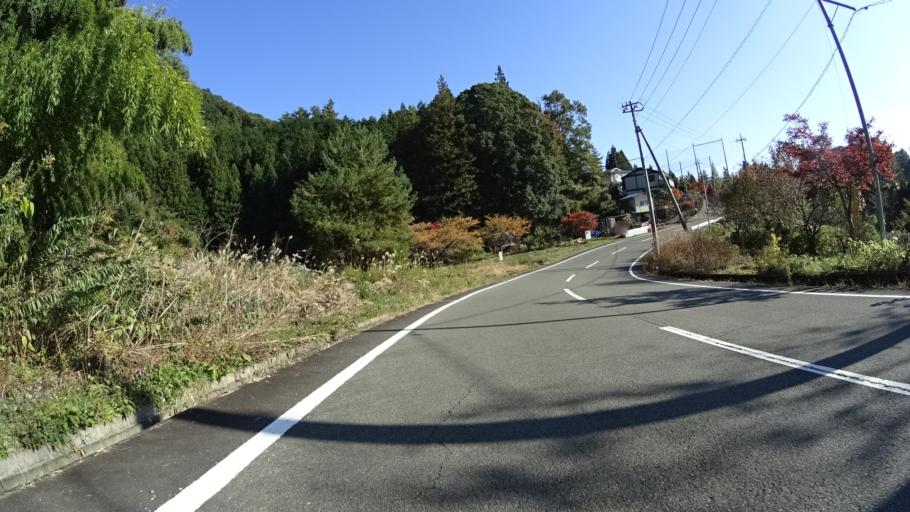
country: JP
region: Yamanashi
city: Uenohara
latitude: 35.6625
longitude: 139.1166
